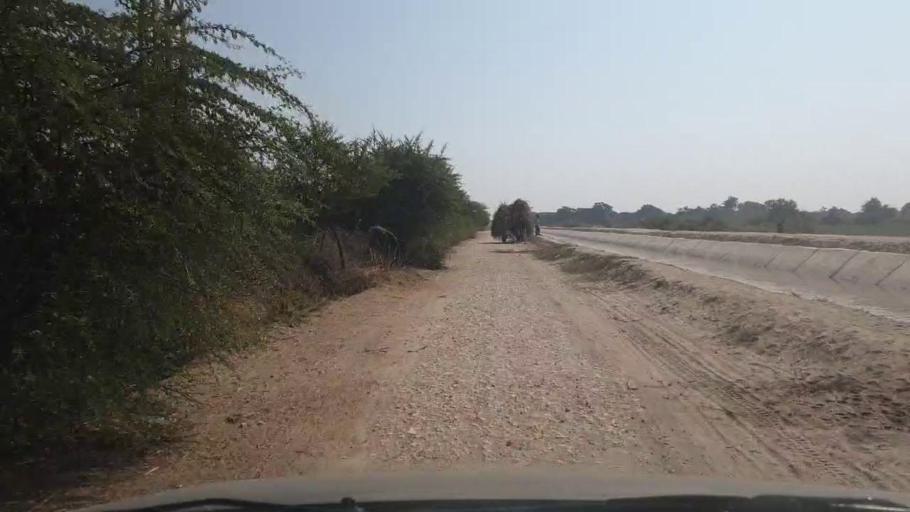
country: PK
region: Sindh
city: Mirwah Gorchani
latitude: 25.2551
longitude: 69.1248
